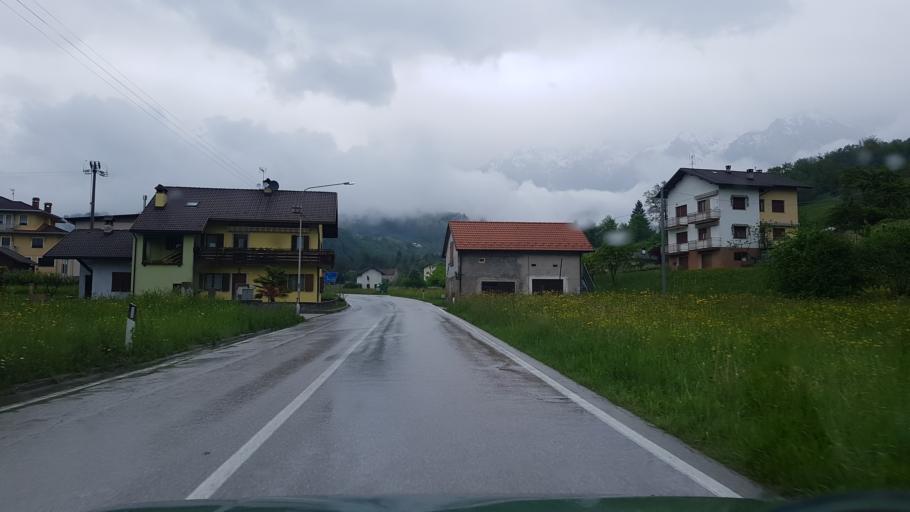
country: IT
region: Veneto
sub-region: Provincia di Belluno
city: Puos d'Alpago
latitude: 46.1454
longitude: 12.3834
